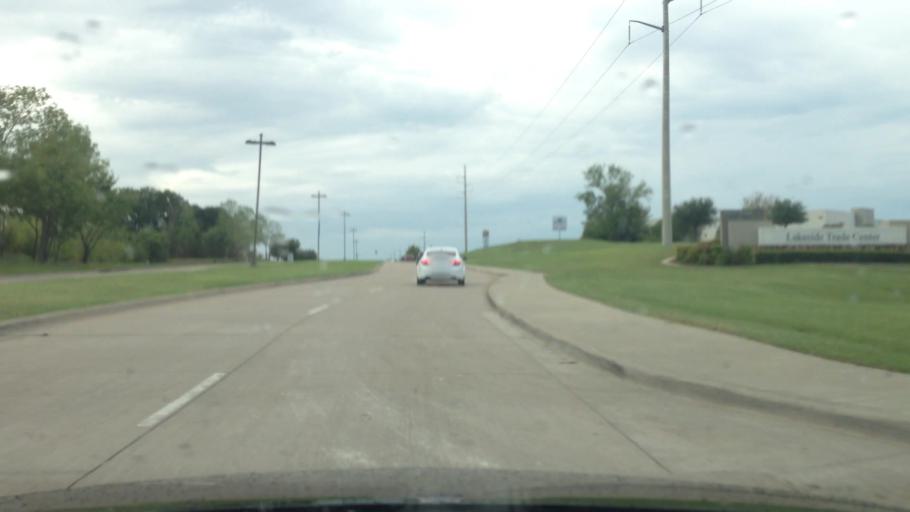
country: US
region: Texas
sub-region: Dallas County
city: Coppell
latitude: 32.9881
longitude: -97.0309
